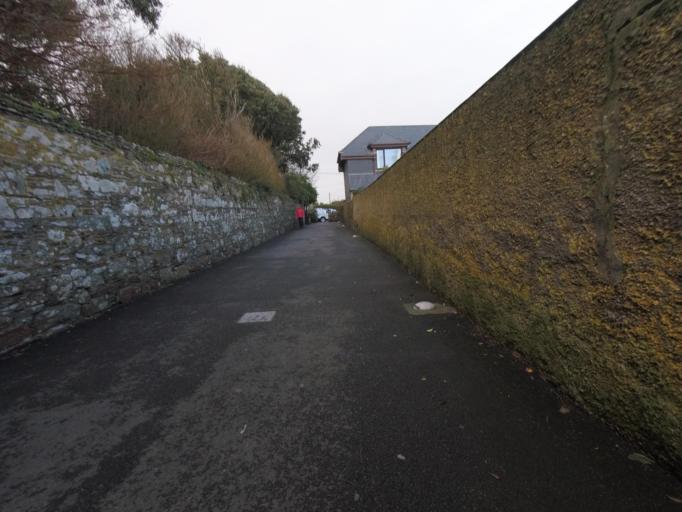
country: IE
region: Munster
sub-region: Waterford
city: Tra Mhor
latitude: 52.1579
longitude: -7.1538
